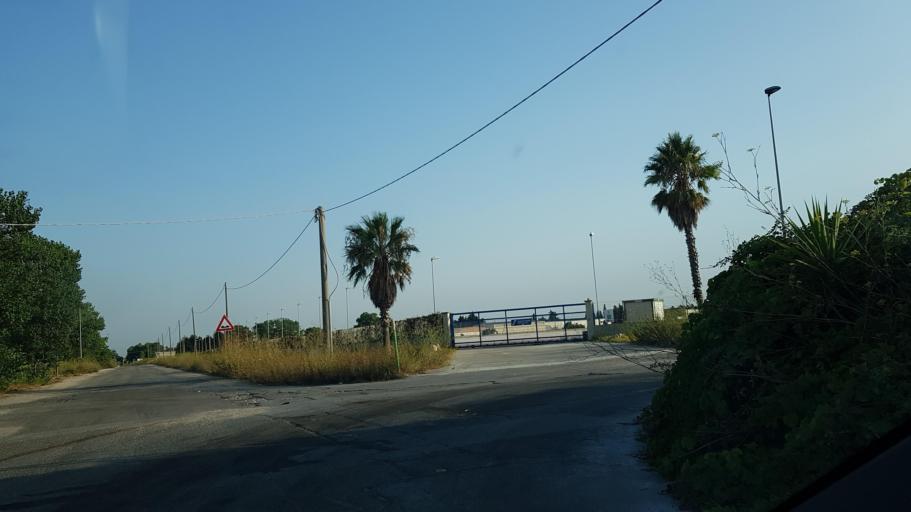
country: IT
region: Apulia
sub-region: Provincia di Brindisi
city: Materdomini
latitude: 40.6385
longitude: 17.9711
